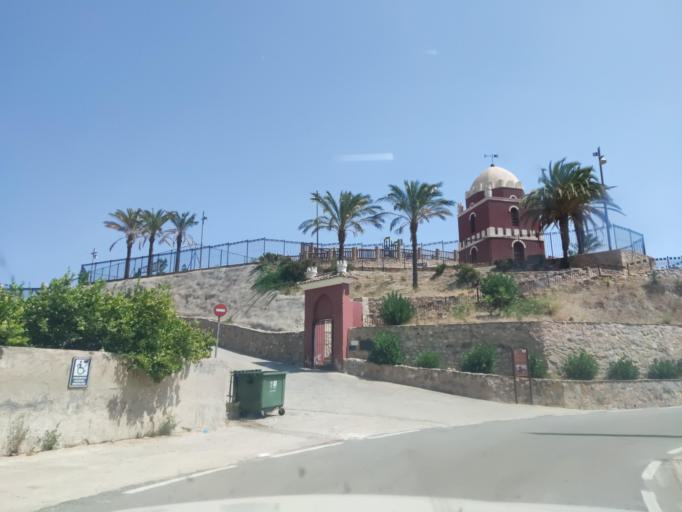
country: ES
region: Murcia
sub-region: Murcia
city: Ulea
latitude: 38.1426
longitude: -1.3210
